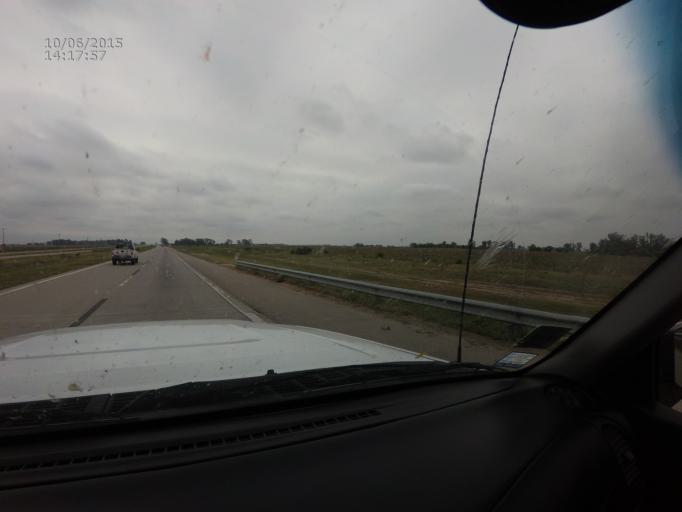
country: AR
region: Cordoba
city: Villa Maria
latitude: -32.3774
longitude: -63.2139
